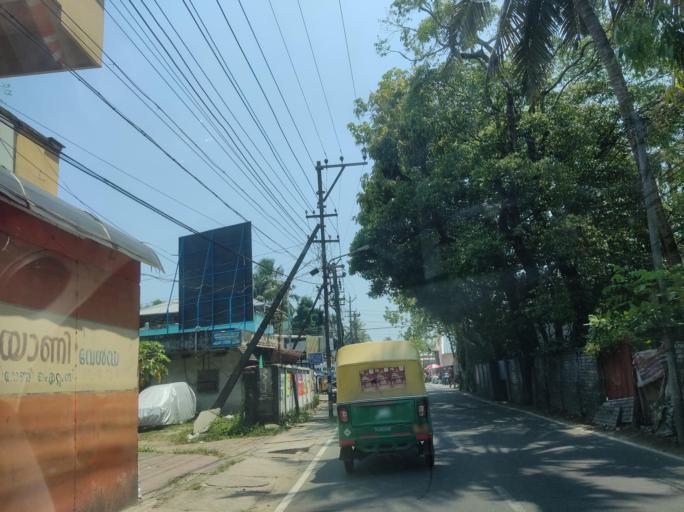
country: IN
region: Kerala
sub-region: Ernakulam
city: Cochin
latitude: 9.9097
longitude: 76.2800
